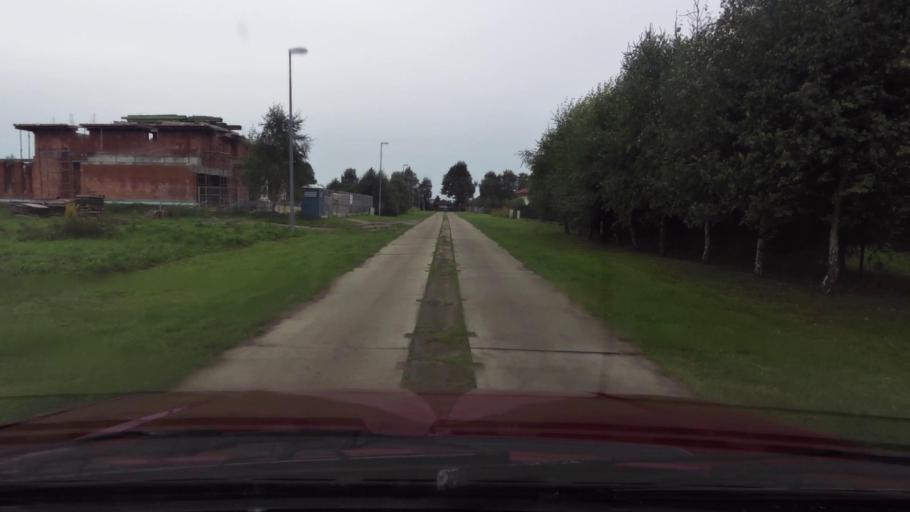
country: PL
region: West Pomeranian Voivodeship
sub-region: Powiat kolobrzeski
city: Grzybowo
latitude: 54.1555
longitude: 15.4887
